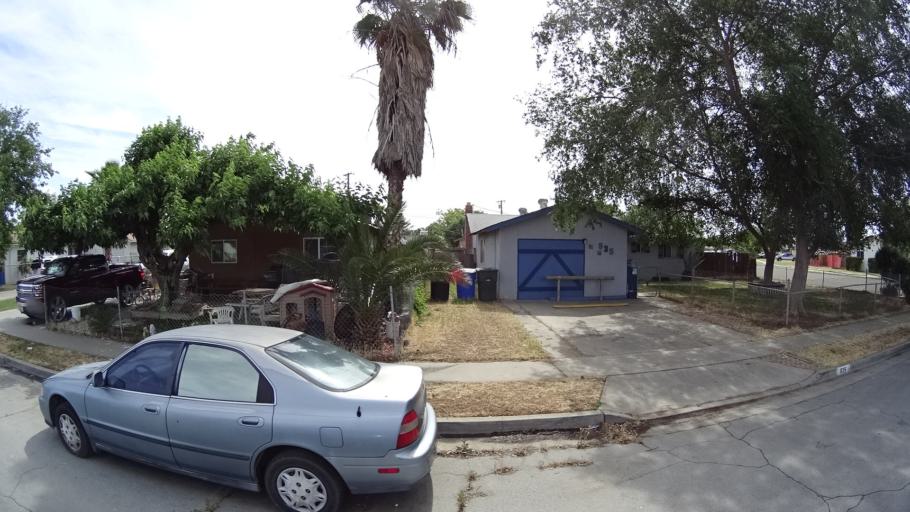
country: US
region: California
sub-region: Kings County
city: Hanford
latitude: 36.3161
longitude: -119.6703
